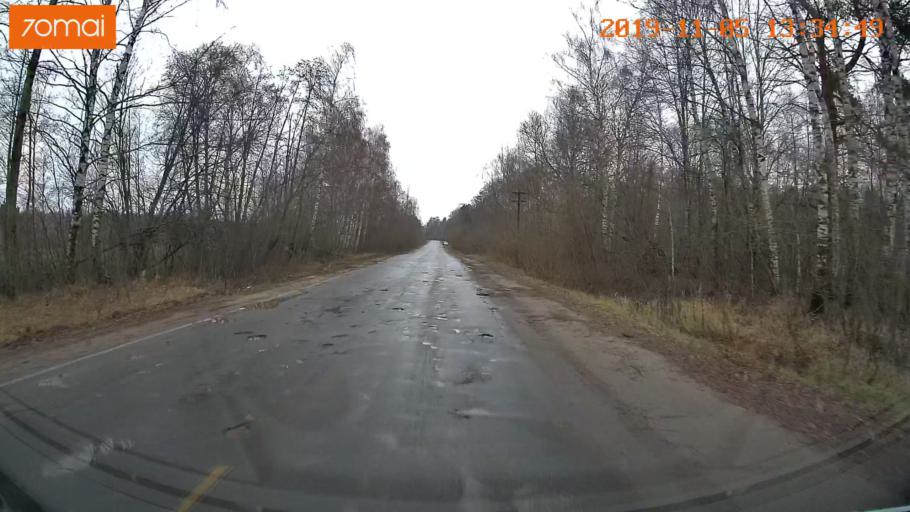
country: RU
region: Ivanovo
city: Shuya
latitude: 56.9036
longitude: 41.3897
